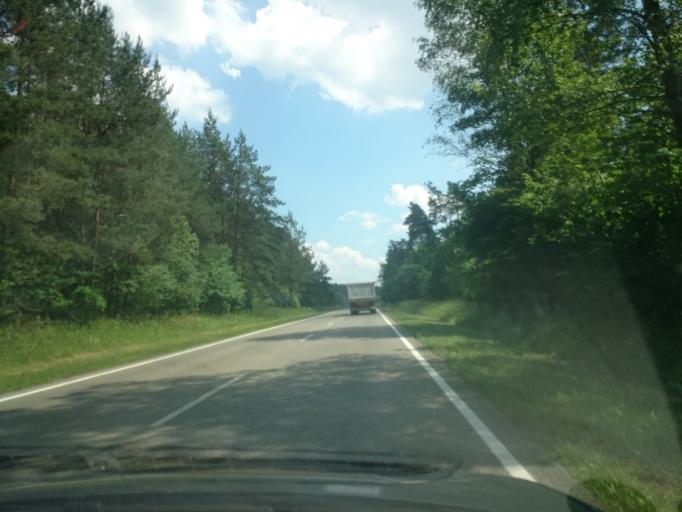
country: DE
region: Bavaria
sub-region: Regierungsbezirk Mittelfranken
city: Hilpoltstein
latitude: 49.2058
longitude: 11.1618
